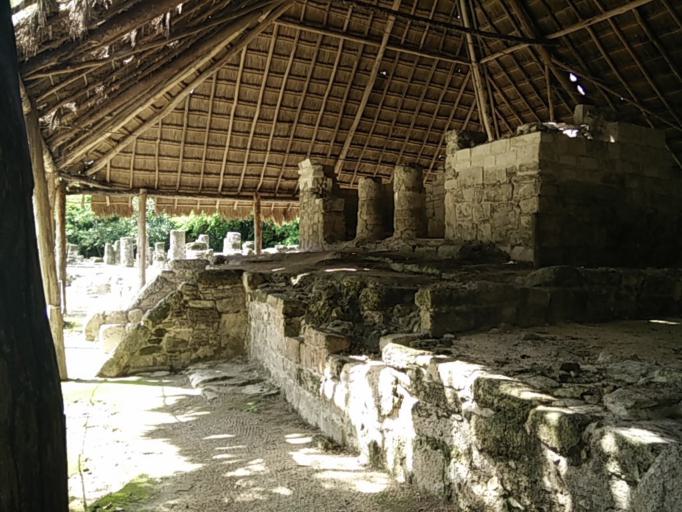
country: MX
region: Quintana Roo
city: San Miguel de Cozumel
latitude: 20.5002
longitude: -86.8464
